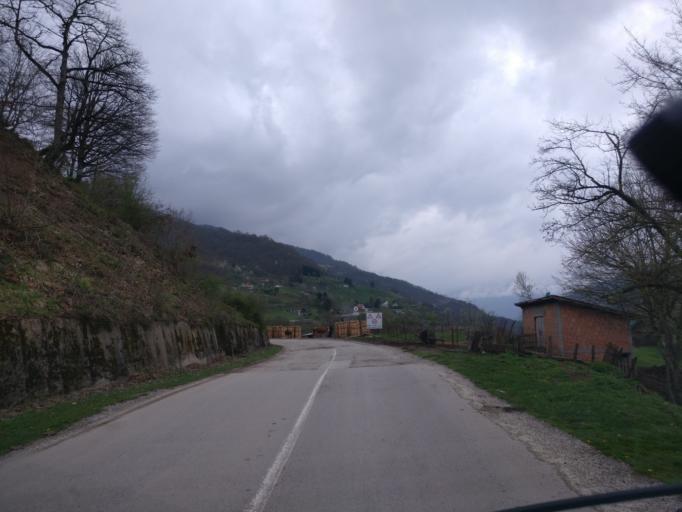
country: BA
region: Republika Srpska
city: Foca
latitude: 43.4410
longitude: 18.7605
